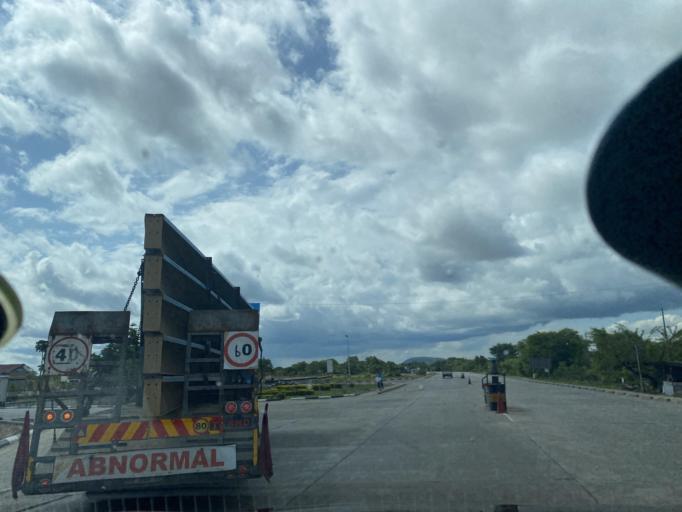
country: ZM
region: Lusaka
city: Kafue
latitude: -15.8489
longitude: 28.2479
